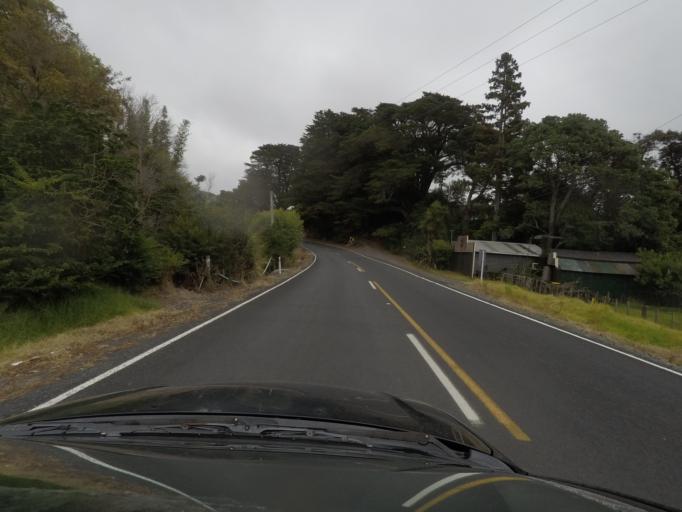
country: NZ
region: Auckland
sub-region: Auckland
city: Warkworth
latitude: -36.2650
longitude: 174.7188
